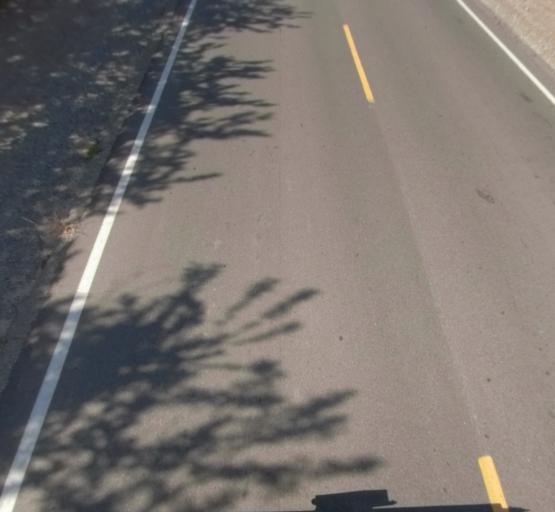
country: US
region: California
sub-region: Madera County
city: Fairmead
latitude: 37.0307
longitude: -120.2569
